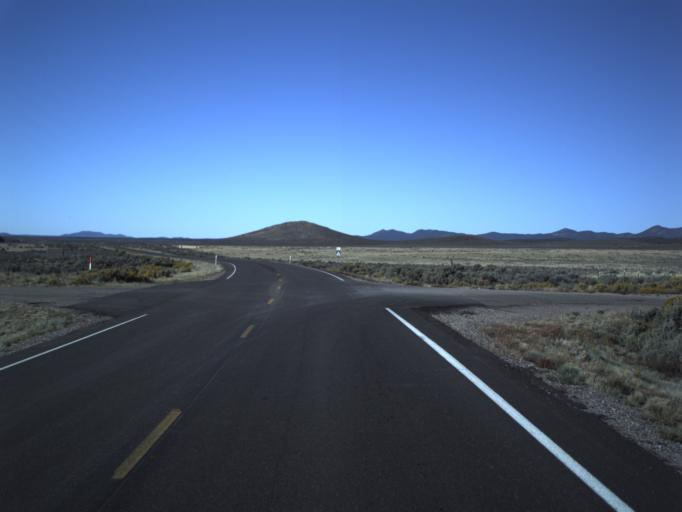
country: US
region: Utah
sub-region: Washington County
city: Enterprise
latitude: 37.8026
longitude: -113.9251
